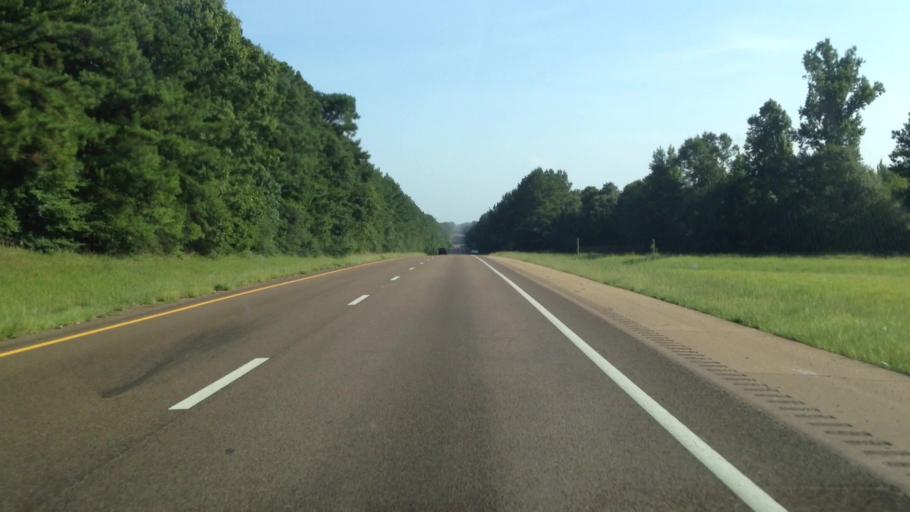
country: US
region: Mississippi
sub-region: Pike County
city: Summit
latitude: 31.3696
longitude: -90.4791
